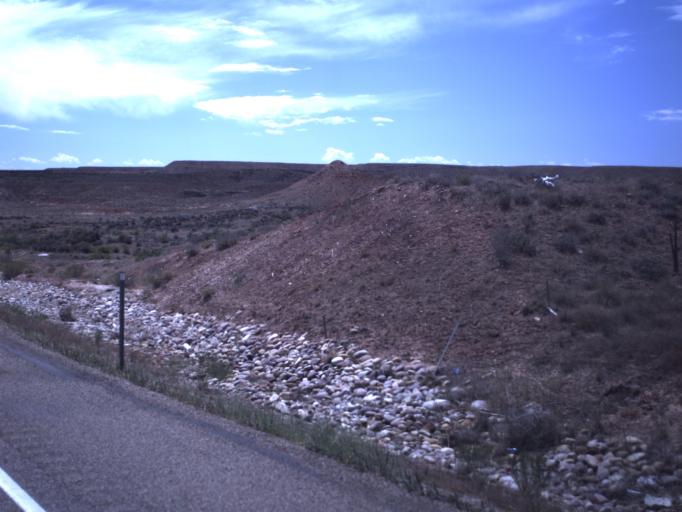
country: US
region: Utah
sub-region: Uintah County
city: Maeser
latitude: 40.3184
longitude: -109.6934
